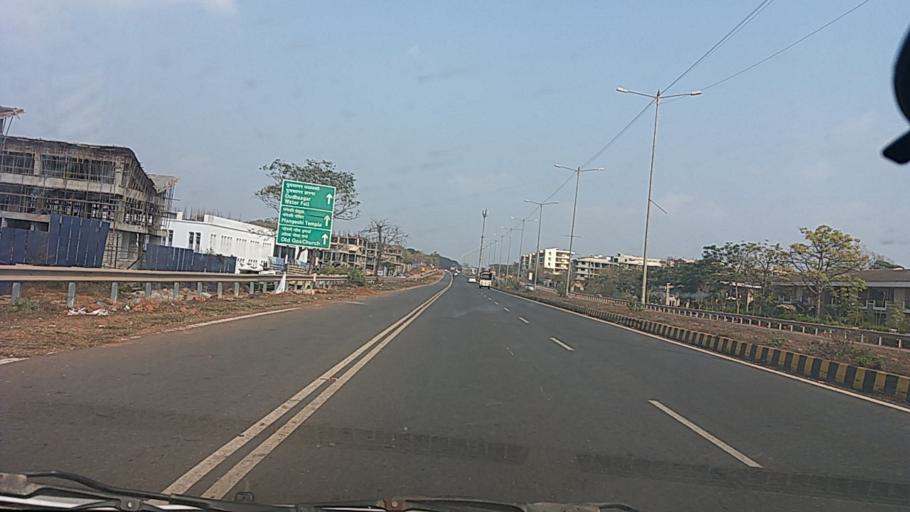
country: IN
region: Goa
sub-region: North Goa
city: Bambolim
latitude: 15.4916
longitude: 73.8892
